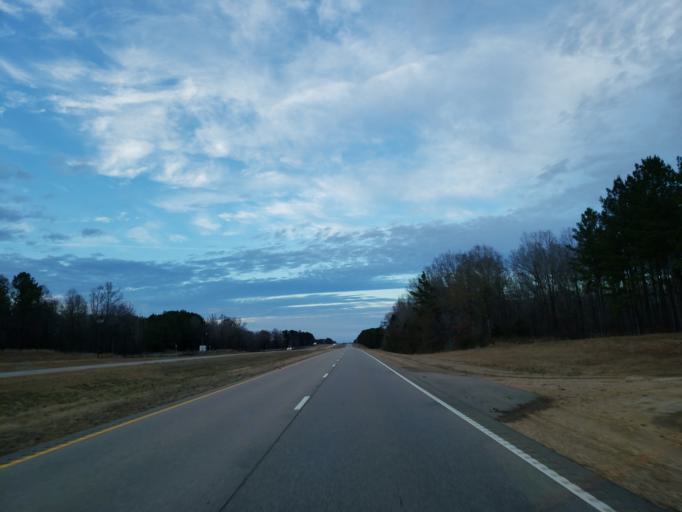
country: US
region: Mississippi
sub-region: Kemper County
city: De Kalb
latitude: 32.7756
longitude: -88.4614
